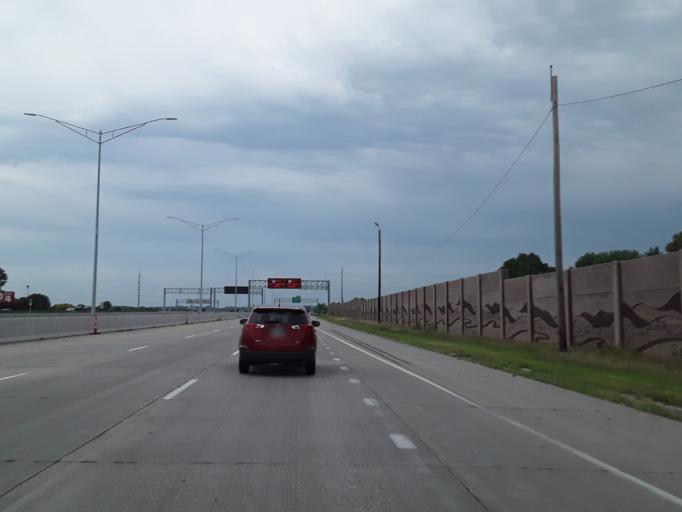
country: US
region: Iowa
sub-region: Pottawattamie County
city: Council Bluffs
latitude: 41.2327
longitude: -95.8604
